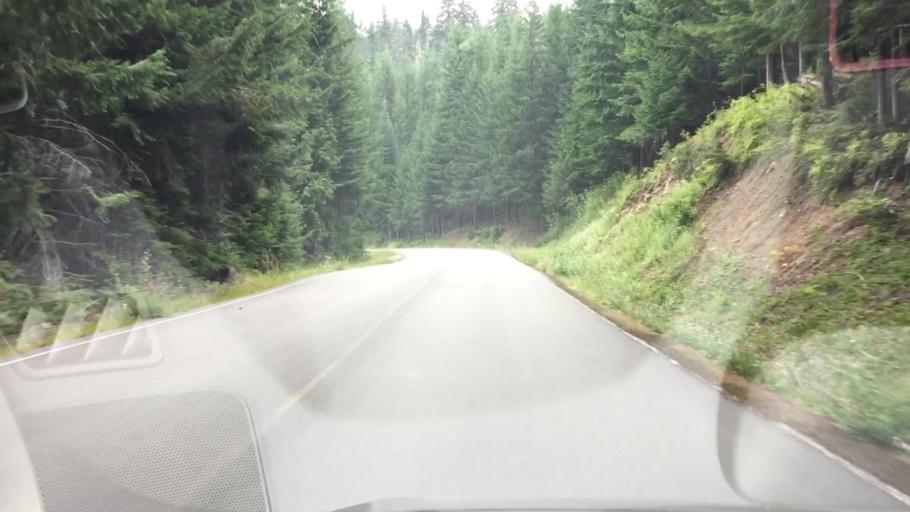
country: US
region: Washington
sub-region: Klickitat County
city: White Salmon
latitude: 46.2098
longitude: -121.6333
